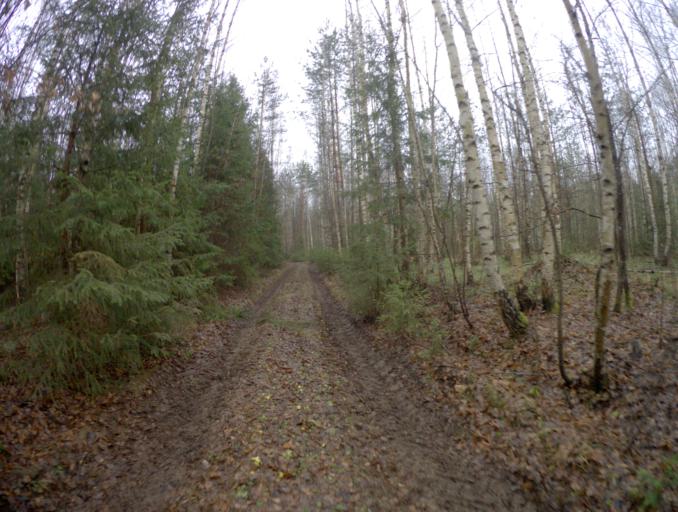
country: RU
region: Vladimir
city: Golovino
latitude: 56.0023
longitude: 40.4709
